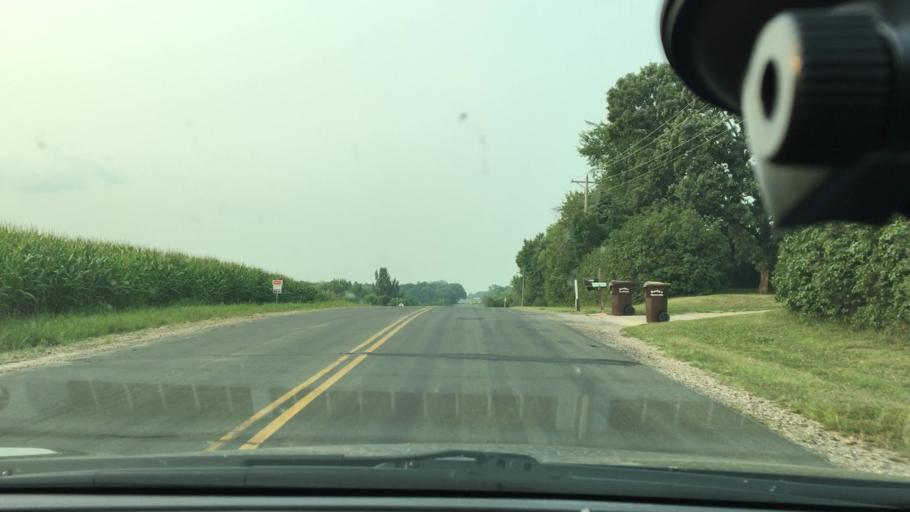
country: US
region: Minnesota
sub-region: Wright County
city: Albertville
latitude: 45.2743
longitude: -93.6841
